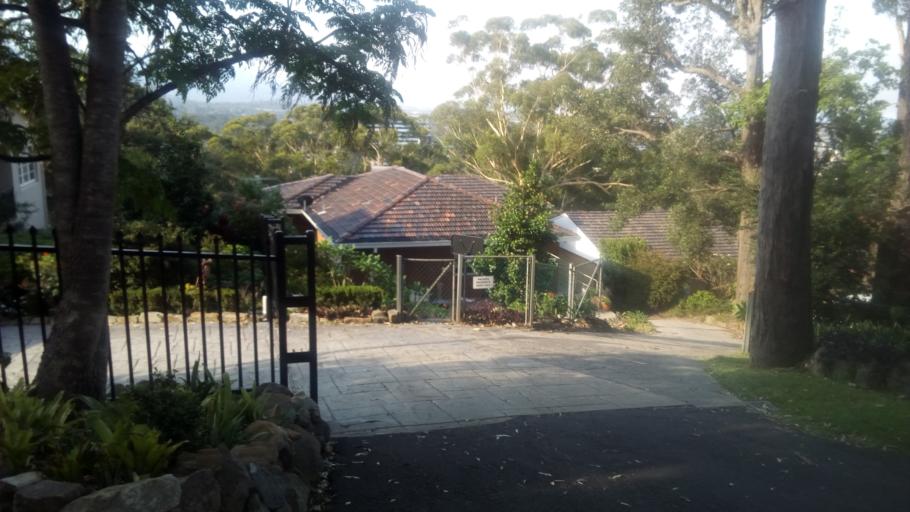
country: AU
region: New South Wales
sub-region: Wollongong
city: Mangerton
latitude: -34.4315
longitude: 150.8791
